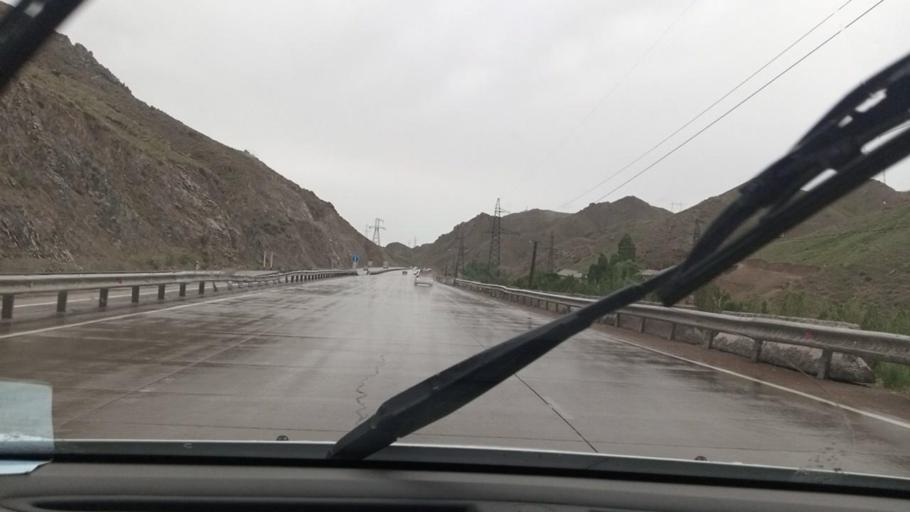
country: TJ
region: Viloyati Sughd
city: Shaydon
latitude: 40.9677
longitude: 70.6564
